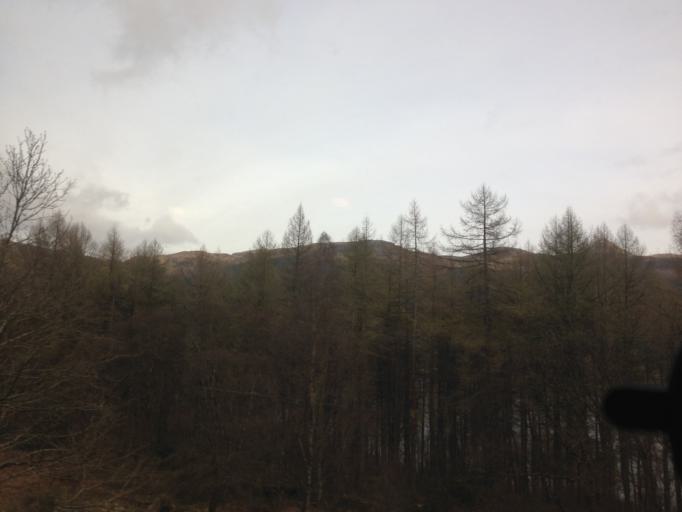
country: GB
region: Scotland
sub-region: Argyll and Bute
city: Garelochhead
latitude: 56.2131
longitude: -4.7012
